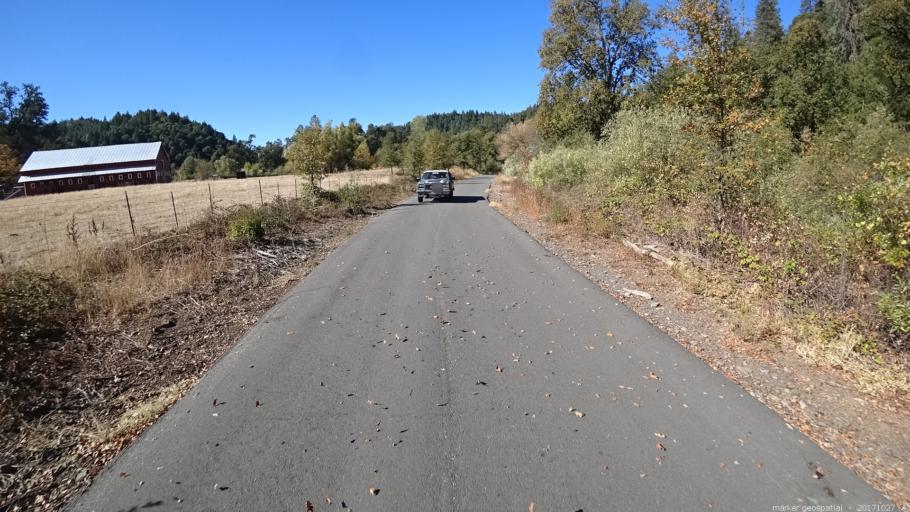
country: US
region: California
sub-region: Shasta County
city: Bella Vista
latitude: 40.7540
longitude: -122.0220
